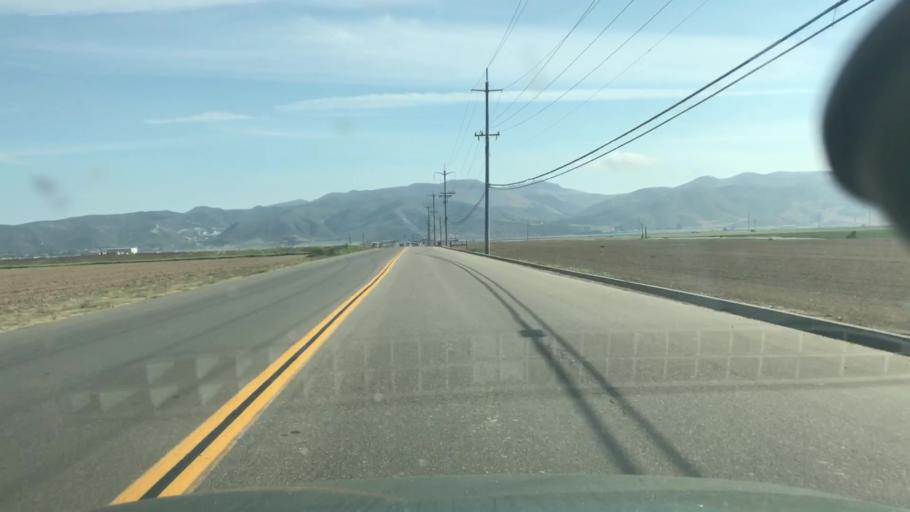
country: US
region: California
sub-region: Santa Barbara County
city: Lompoc
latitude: 34.6688
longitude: -120.4927
